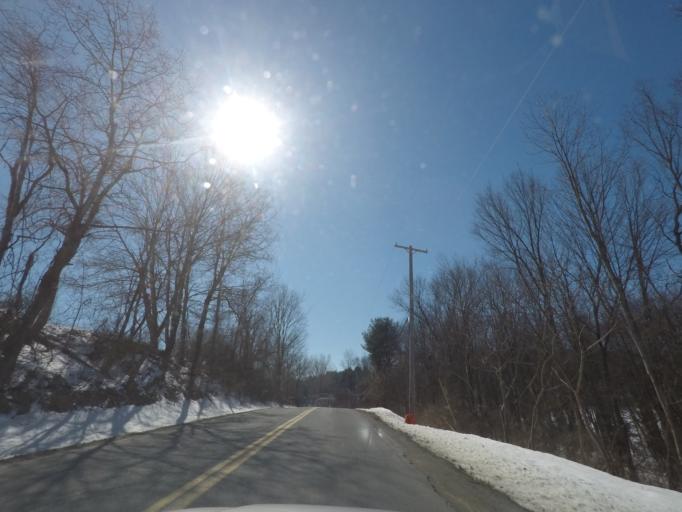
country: US
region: New York
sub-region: Saratoga County
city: Stillwater
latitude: 42.8933
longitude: -73.5700
